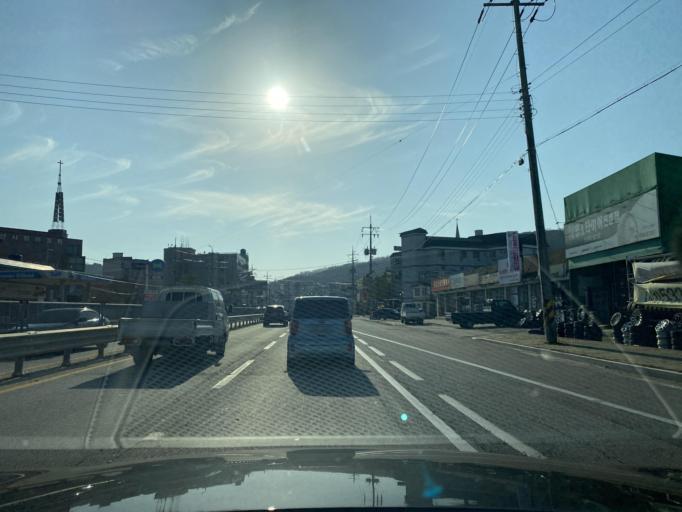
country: KR
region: Chungcheongnam-do
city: Asan
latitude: 36.7784
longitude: 126.9362
